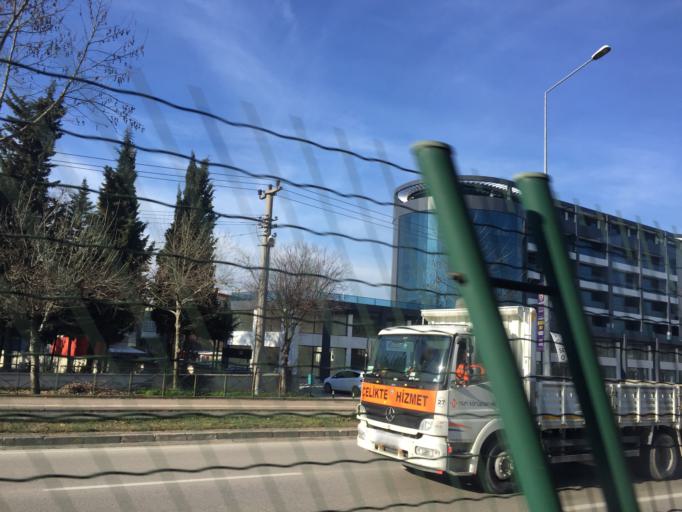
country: TR
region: Bursa
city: Yildirim
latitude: 40.2175
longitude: 28.9995
